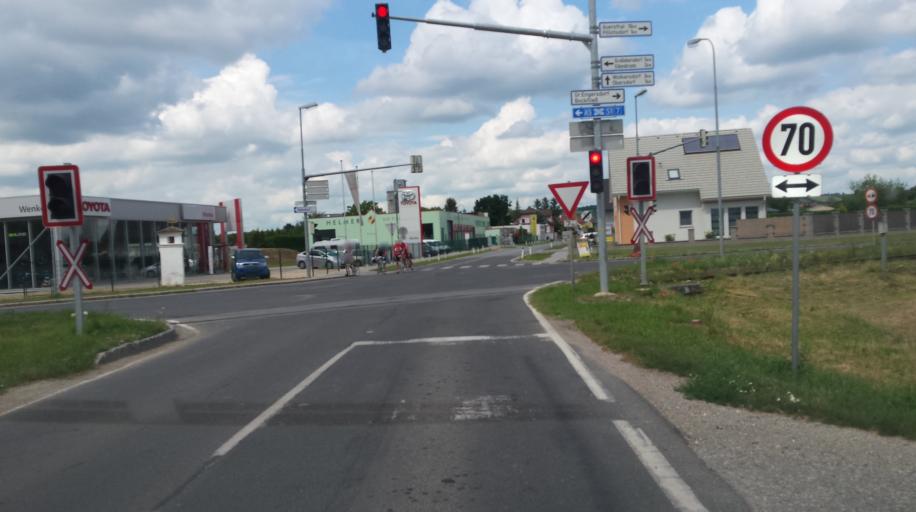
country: AT
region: Lower Austria
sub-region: Politischer Bezirk Mistelbach
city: Pillichsdorf
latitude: 48.3626
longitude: 16.5226
